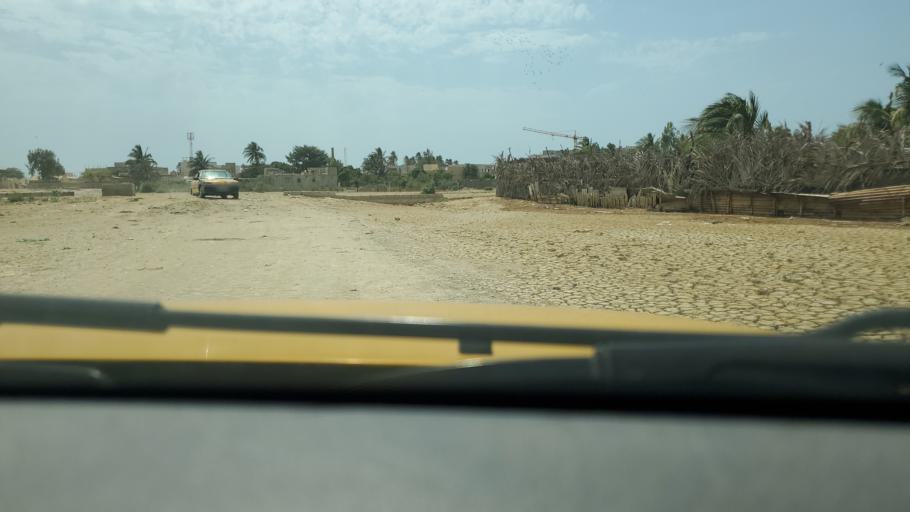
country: SN
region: Saint-Louis
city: Saint-Louis
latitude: 16.0260
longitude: -16.4716
